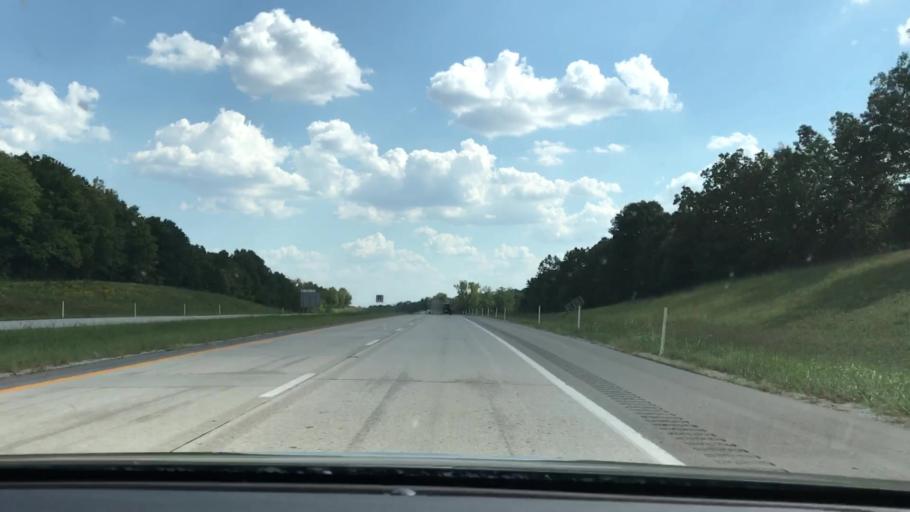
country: US
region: Kentucky
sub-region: Ohio County
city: Oak Grove
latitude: 37.3722
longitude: -86.8020
